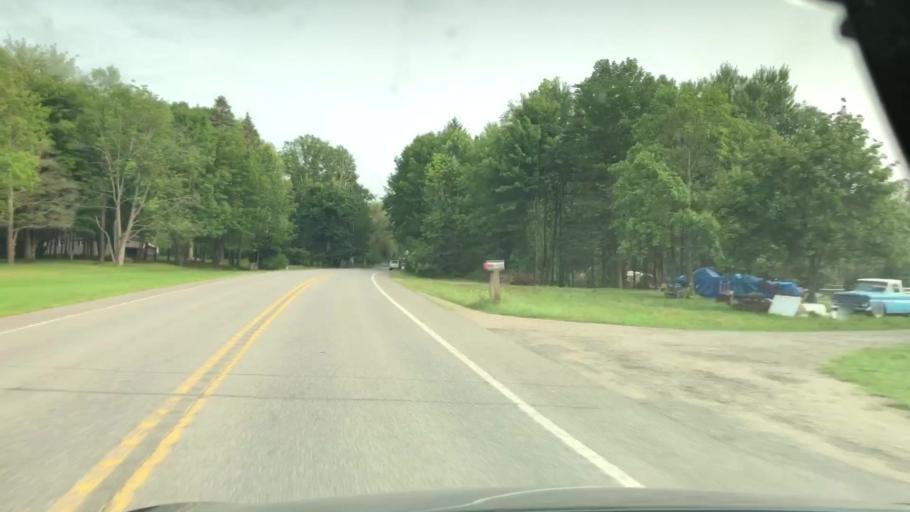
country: US
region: Pennsylvania
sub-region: Erie County
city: Union City
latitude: 41.8283
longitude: -79.8124
